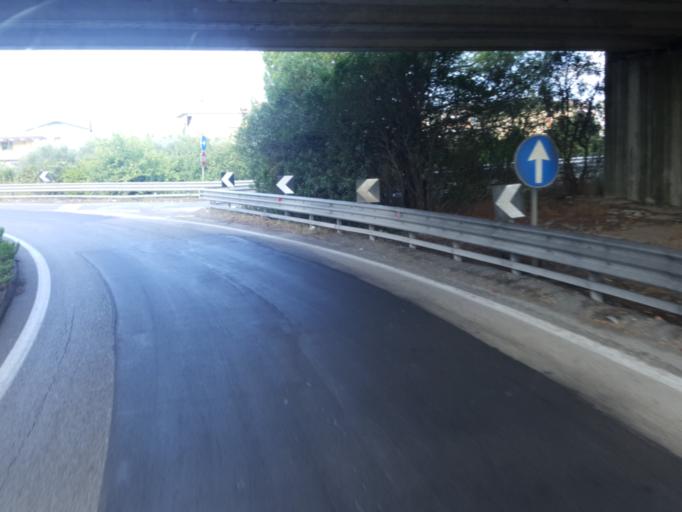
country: IT
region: Tuscany
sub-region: Provincia di Livorno
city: Venturina
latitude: 43.0171
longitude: 10.5993
